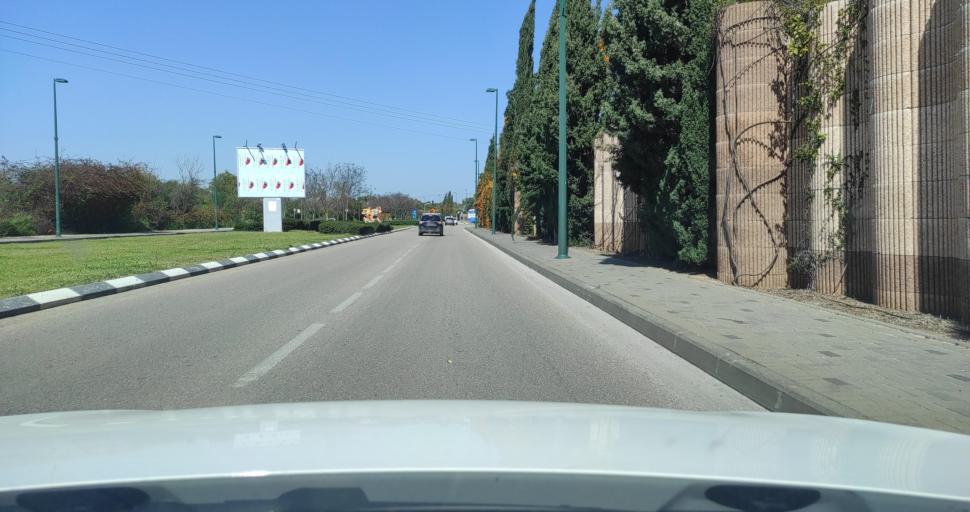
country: IL
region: Central District
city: Bet Yizhaq
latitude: 32.3160
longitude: 34.8804
